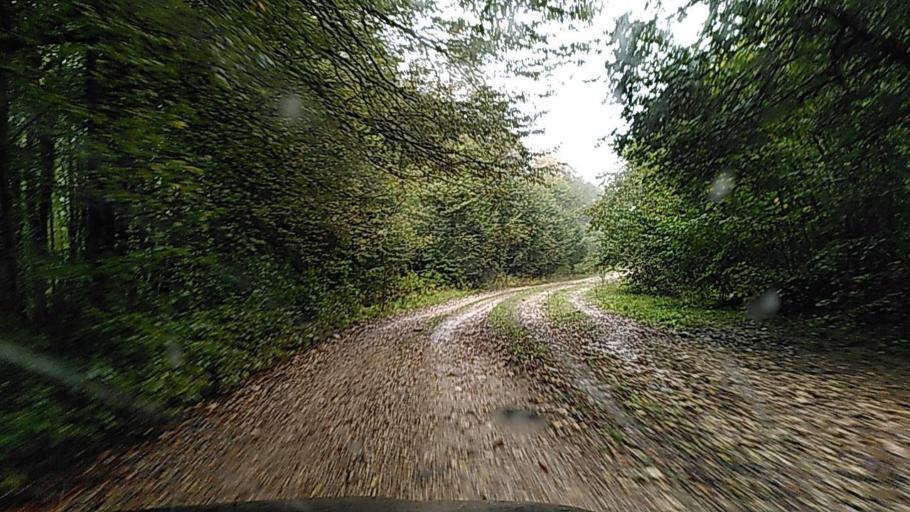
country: RU
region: Kabardino-Balkariya
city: Belaya Rechka
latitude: 43.3940
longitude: 43.4442
